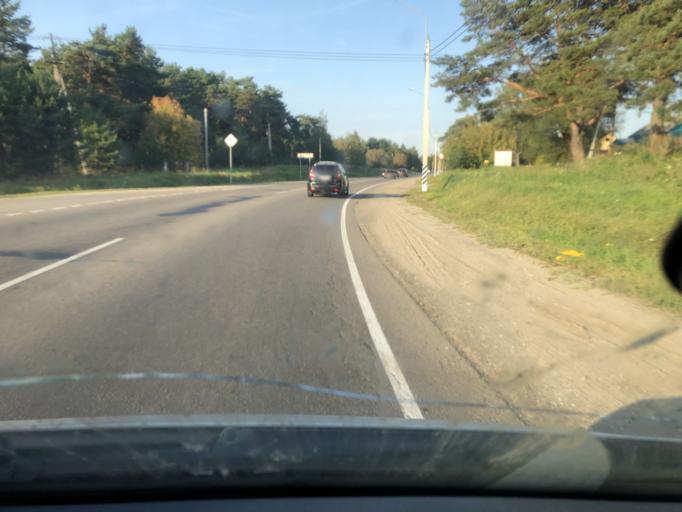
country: RU
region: Kaluga
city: Peremyshl'
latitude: 54.3394
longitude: 36.1836
